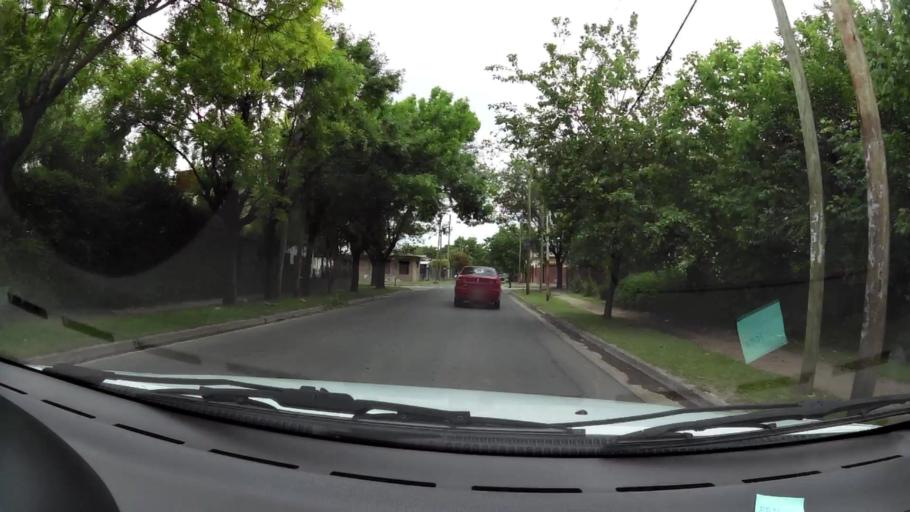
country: AR
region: Buenos Aires
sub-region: Partido de Ezeiza
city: Ezeiza
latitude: -34.8436
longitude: -58.5113
